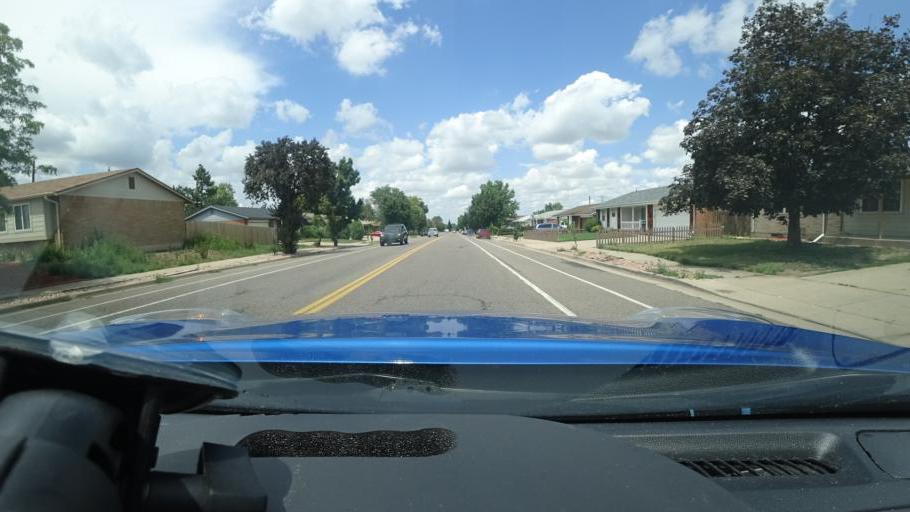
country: US
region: Colorado
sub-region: Adams County
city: Aurora
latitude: 39.7014
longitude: -104.8301
